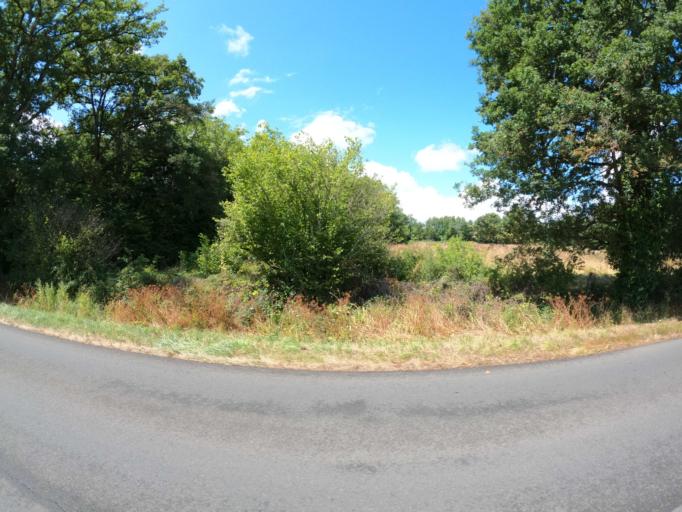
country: FR
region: Pays de la Loire
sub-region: Departement de Maine-et-Loire
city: Champigne
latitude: 47.6376
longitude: -0.5792
